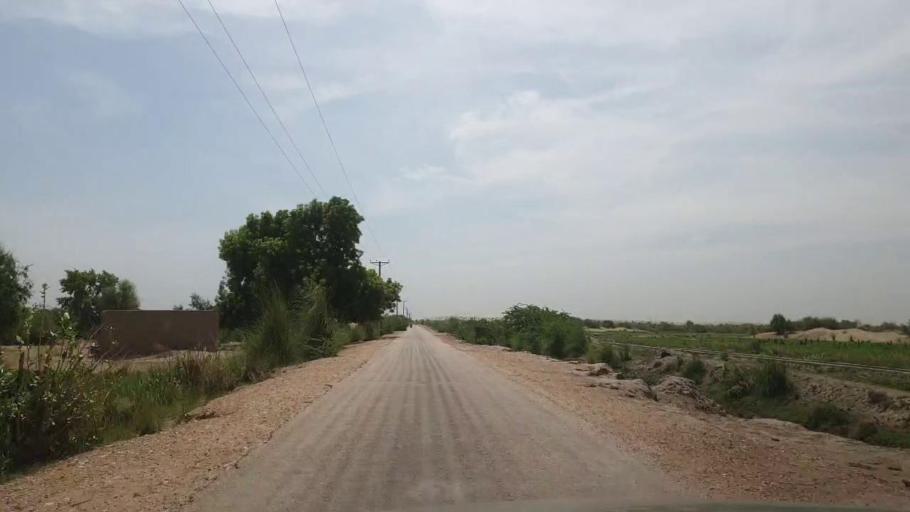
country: PK
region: Sindh
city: Kot Diji
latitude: 27.1178
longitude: 69.0077
